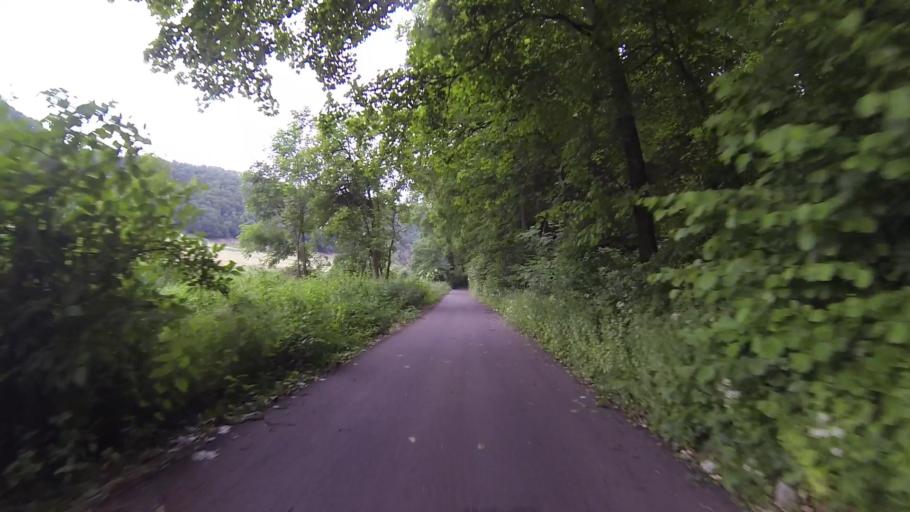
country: DE
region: Baden-Wuerttemberg
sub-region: Tuebingen Region
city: Blaubeuren
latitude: 48.4058
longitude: 9.8368
